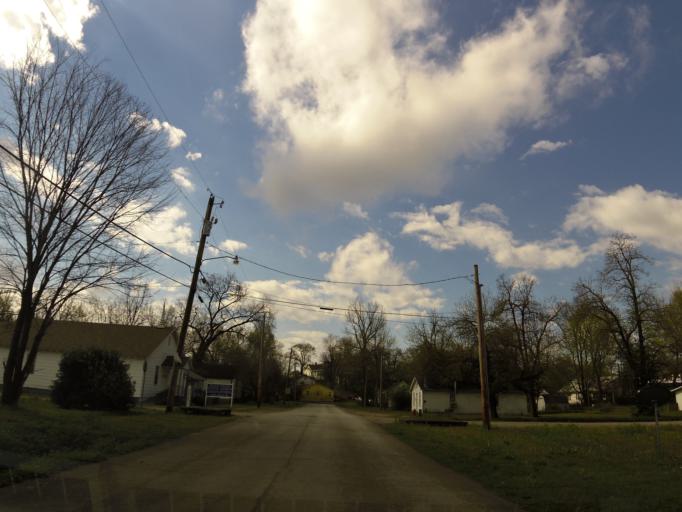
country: US
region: Missouri
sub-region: Butler County
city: Poplar Bluff
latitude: 36.7636
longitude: -90.3918
